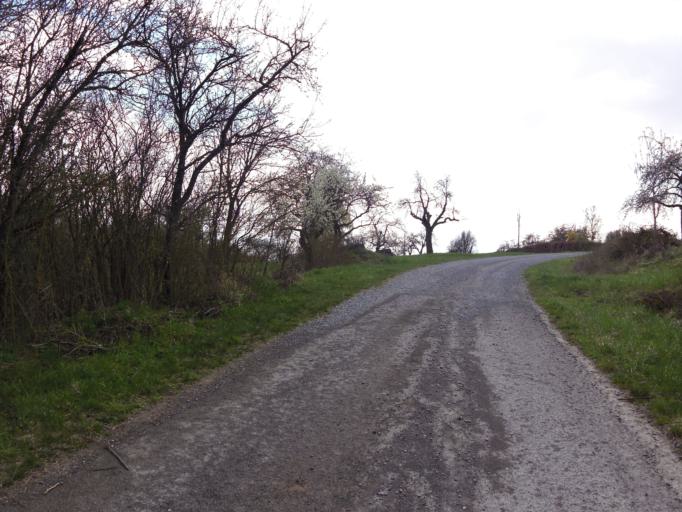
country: DE
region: Bavaria
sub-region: Regierungsbezirk Unterfranken
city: Rimpar
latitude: 49.8637
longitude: 9.9563
